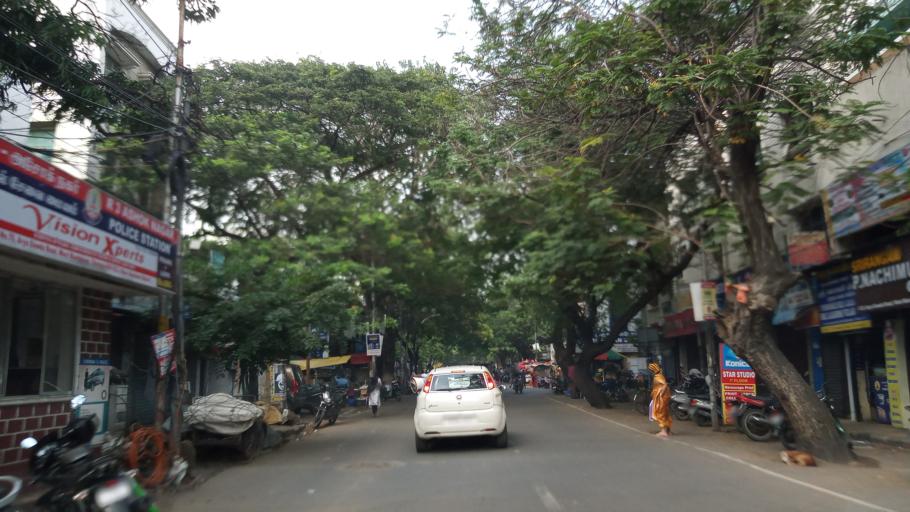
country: IN
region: Tamil Nadu
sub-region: Chennai
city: Chetput
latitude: 13.0391
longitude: 80.2212
